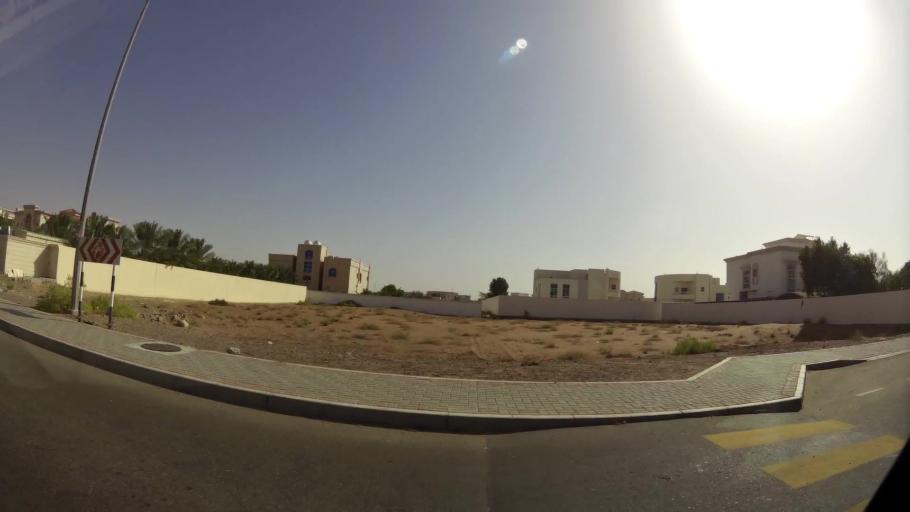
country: OM
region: Al Buraimi
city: Al Buraymi
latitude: 24.3496
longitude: 55.7953
